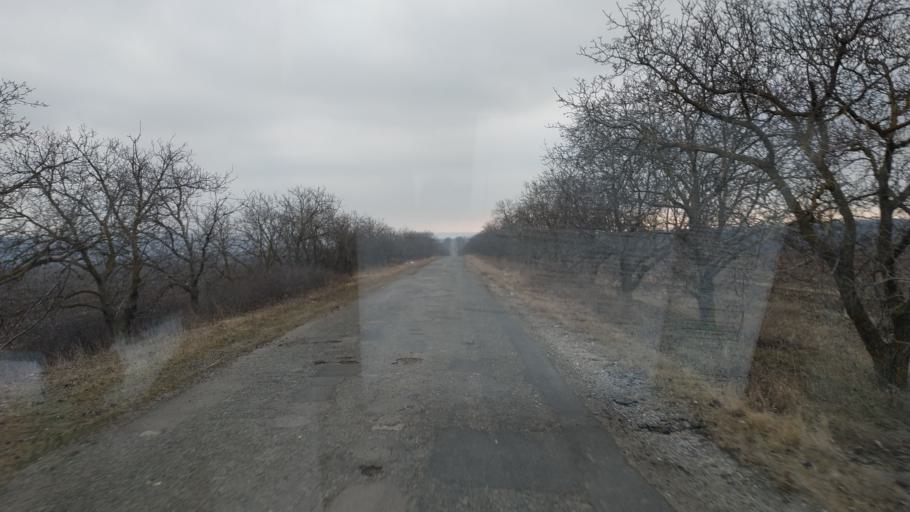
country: MD
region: Hincesti
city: Dancu
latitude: 46.8785
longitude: 28.2974
